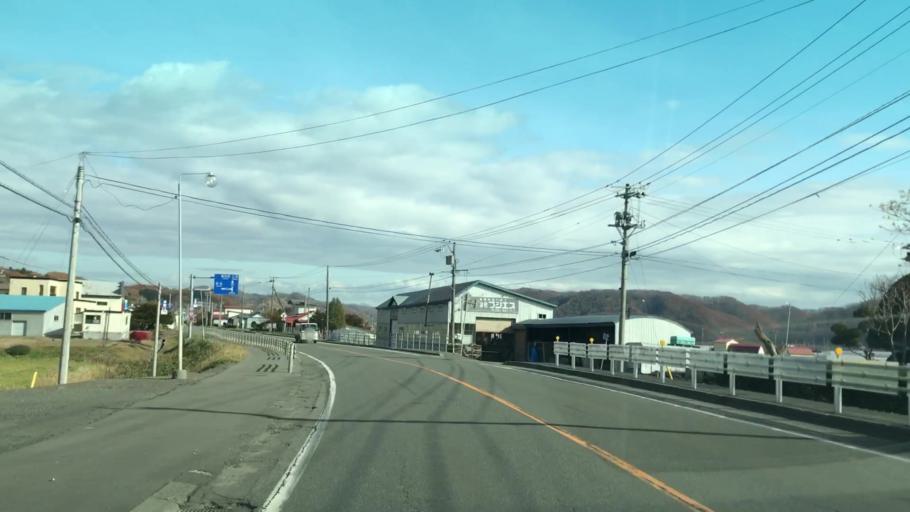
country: JP
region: Hokkaido
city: Shizunai-furukawacho
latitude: 42.5783
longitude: 142.1180
